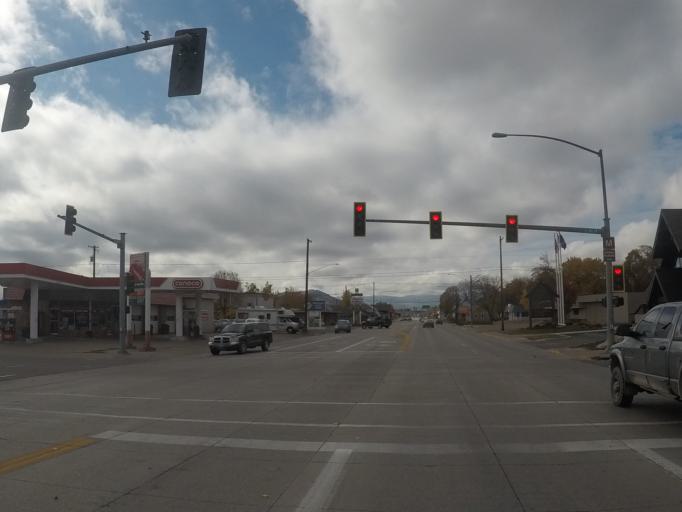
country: US
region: Montana
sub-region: Flathead County
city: Kalispell
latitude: 48.2030
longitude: -114.3098
